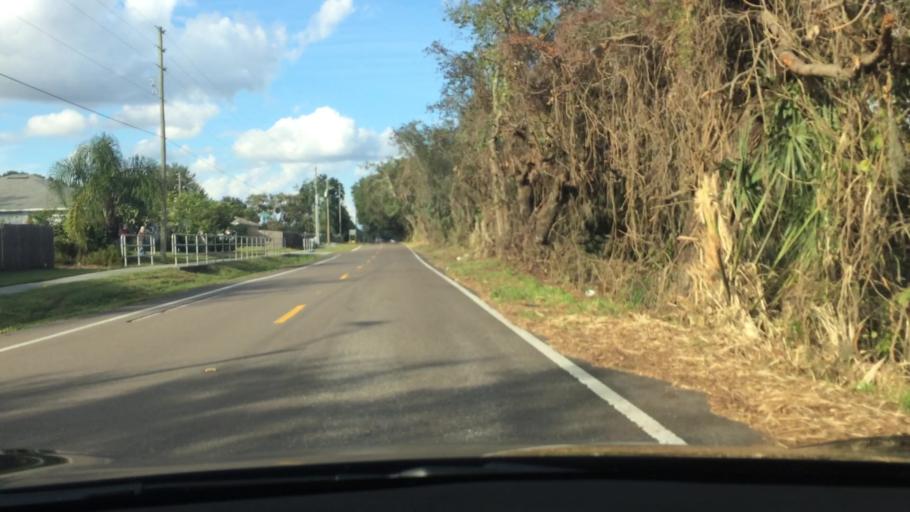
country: US
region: Florida
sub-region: Hillsborough County
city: Lutz
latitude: 28.1774
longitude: -82.4032
